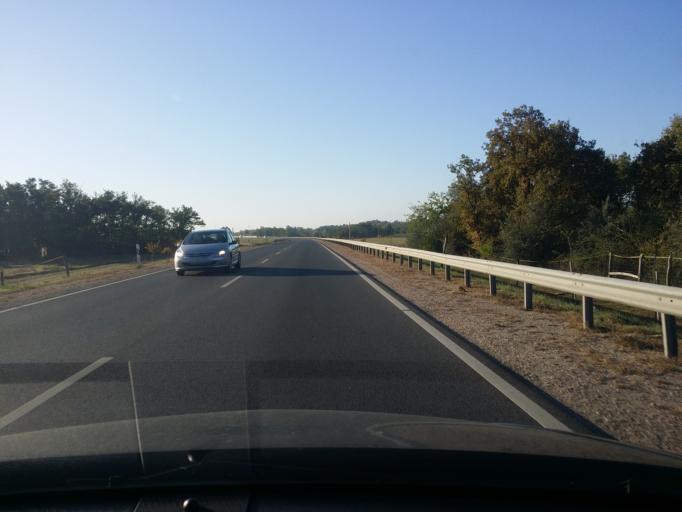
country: HU
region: Bacs-Kiskun
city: Kecskemet
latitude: 46.9322
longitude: 19.7141
